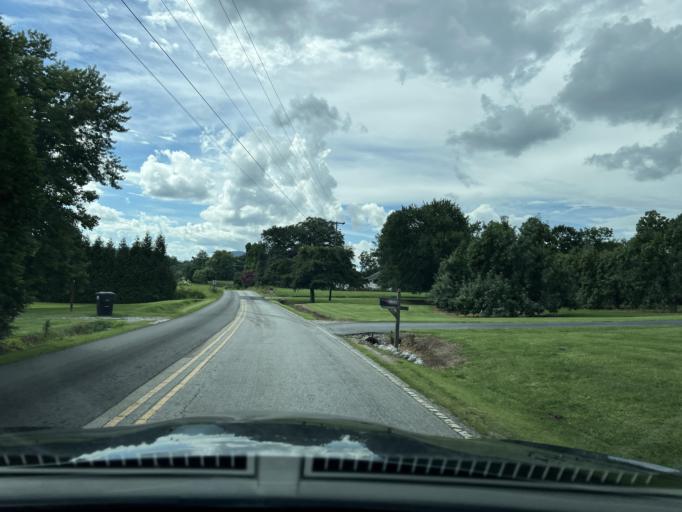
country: US
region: North Carolina
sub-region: Henderson County
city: Edneyville
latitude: 35.3908
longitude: -82.3634
